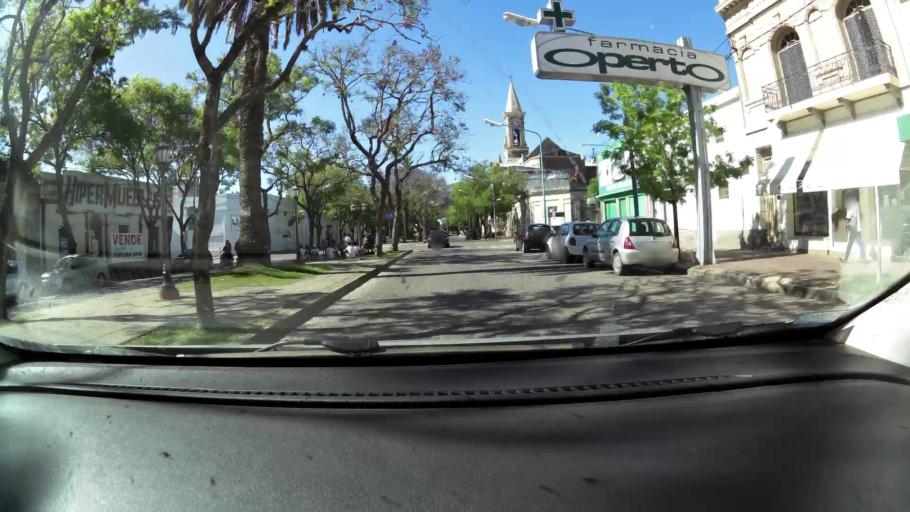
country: AR
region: Santa Fe
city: Rafaela
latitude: -31.2548
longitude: -61.4923
